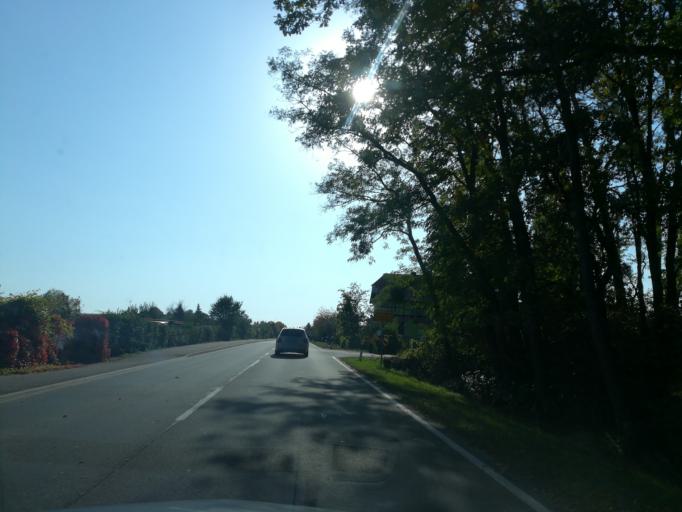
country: DE
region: Saxony-Anhalt
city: Gommern
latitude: 52.0847
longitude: 11.8122
